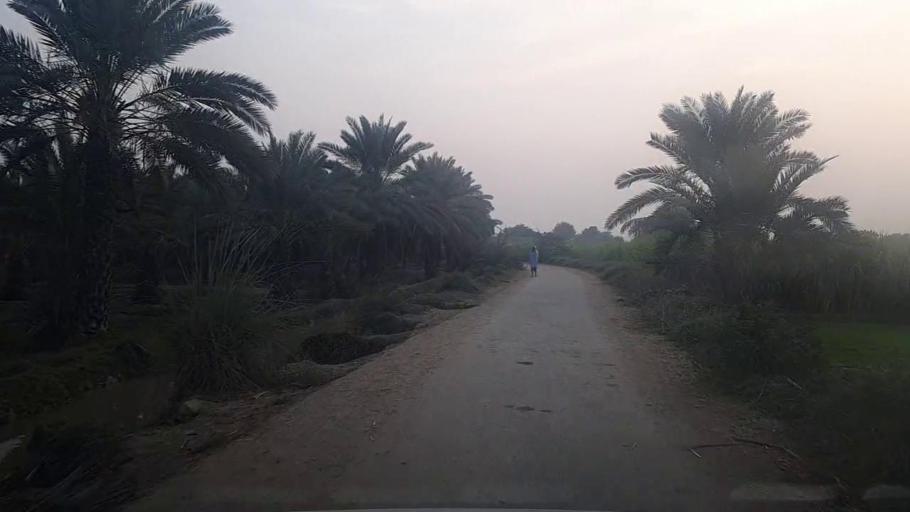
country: PK
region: Sindh
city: Kot Diji
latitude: 27.3408
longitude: 68.6425
